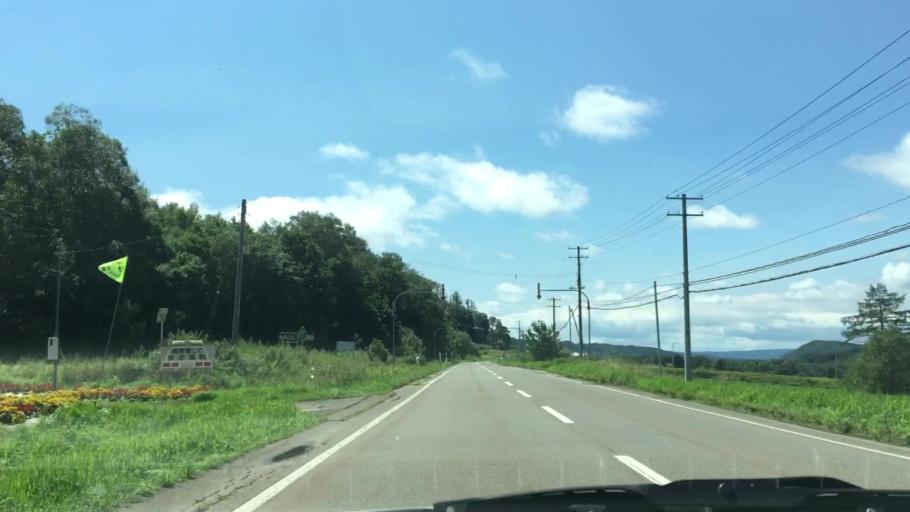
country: JP
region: Hokkaido
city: Kitami
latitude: 43.3160
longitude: 143.7206
